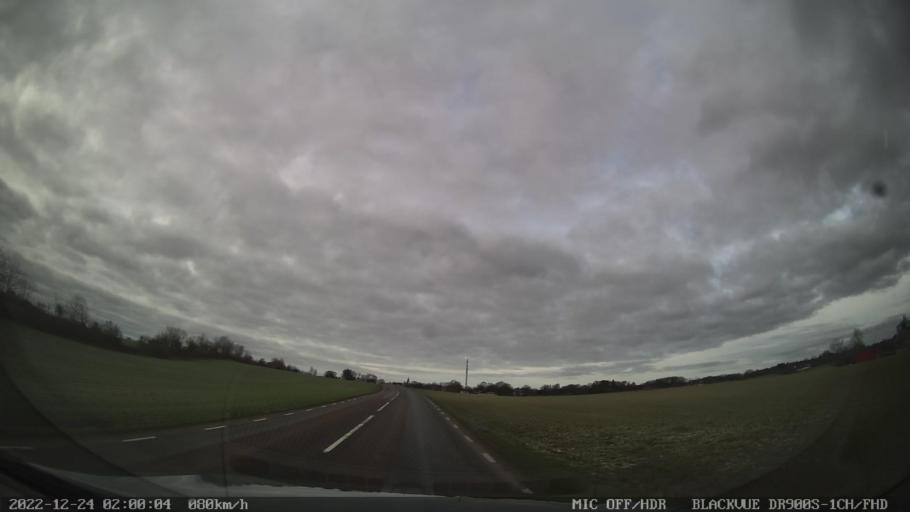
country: SE
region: Skane
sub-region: Tomelilla Kommun
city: Tomelilla
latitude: 55.6112
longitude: 14.0044
